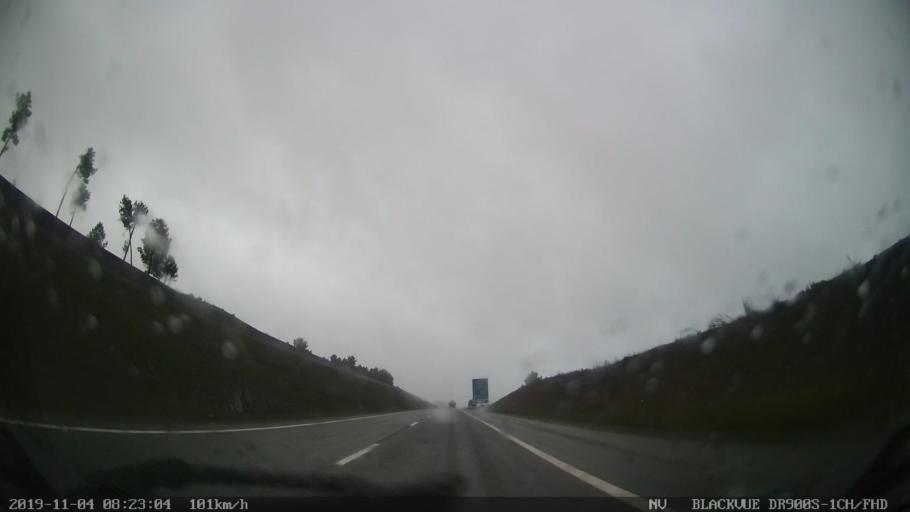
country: PT
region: Vila Real
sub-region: Vila Real
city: Vila Real
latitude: 41.3109
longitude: -7.6877
